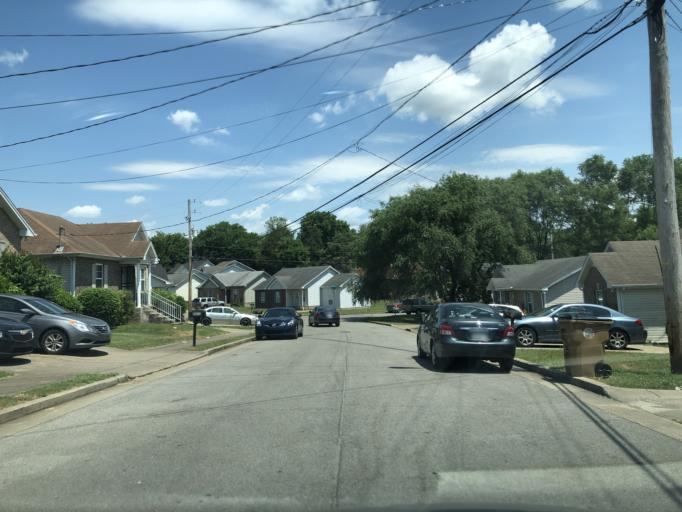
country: US
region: Tennessee
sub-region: Davidson County
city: Goodlettsville
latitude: 36.2684
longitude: -86.7186
